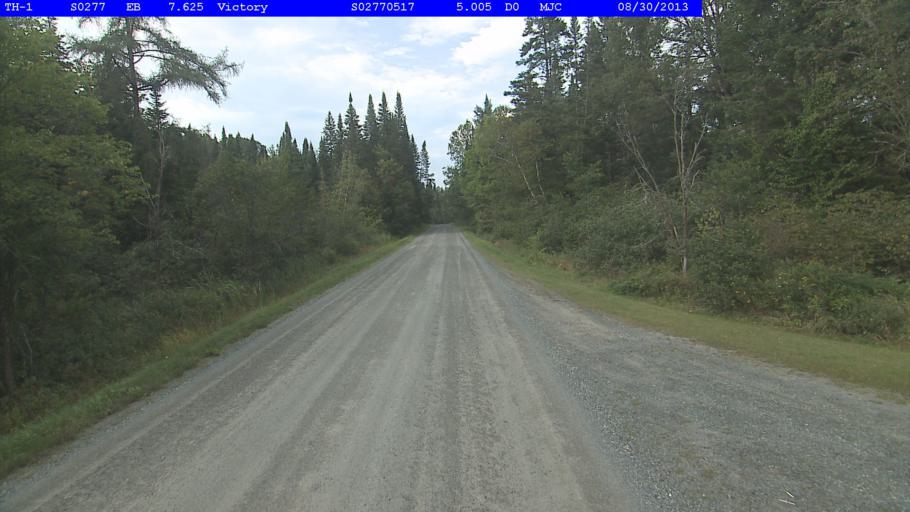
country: US
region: Vermont
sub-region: Caledonia County
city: Lyndonville
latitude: 44.5413
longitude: -71.7870
